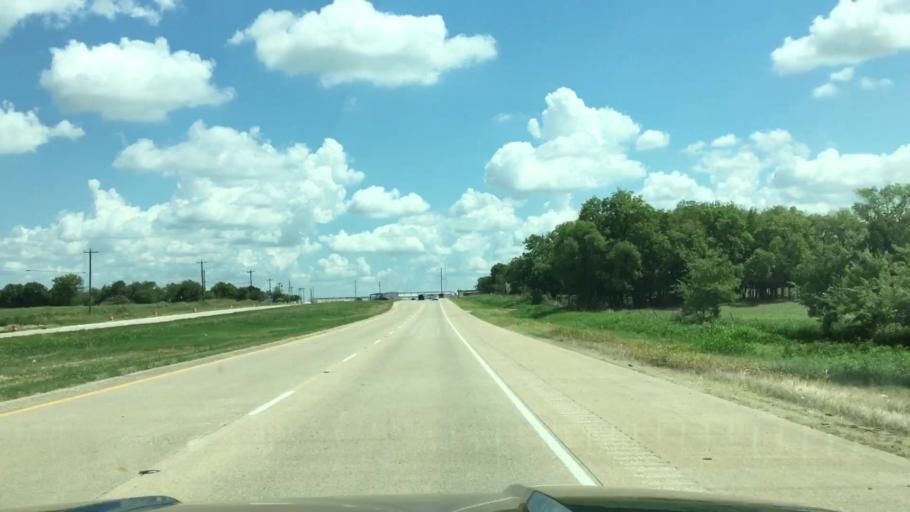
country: US
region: Texas
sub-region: Wise County
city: Rhome
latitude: 33.0399
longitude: -97.4459
